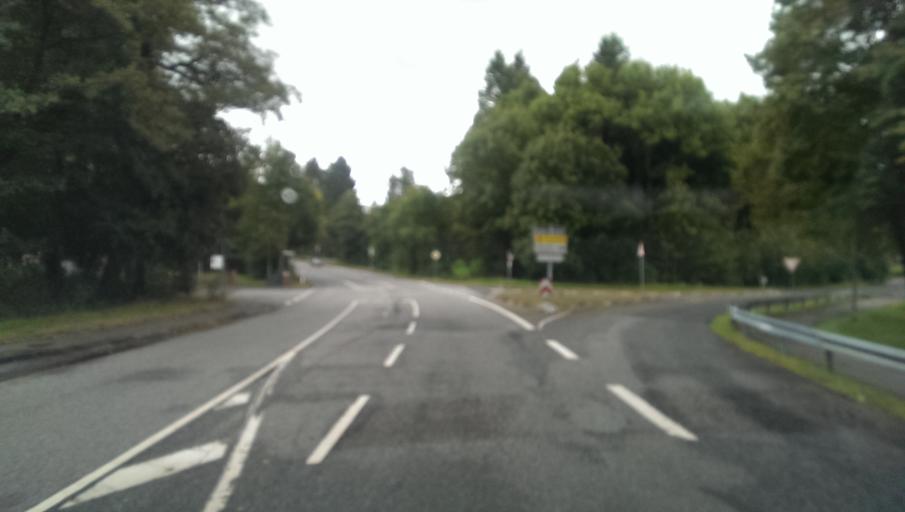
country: DE
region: Hesse
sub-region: Regierungsbezirk Giessen
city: Grunberg
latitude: 50.5908
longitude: 8.9809
